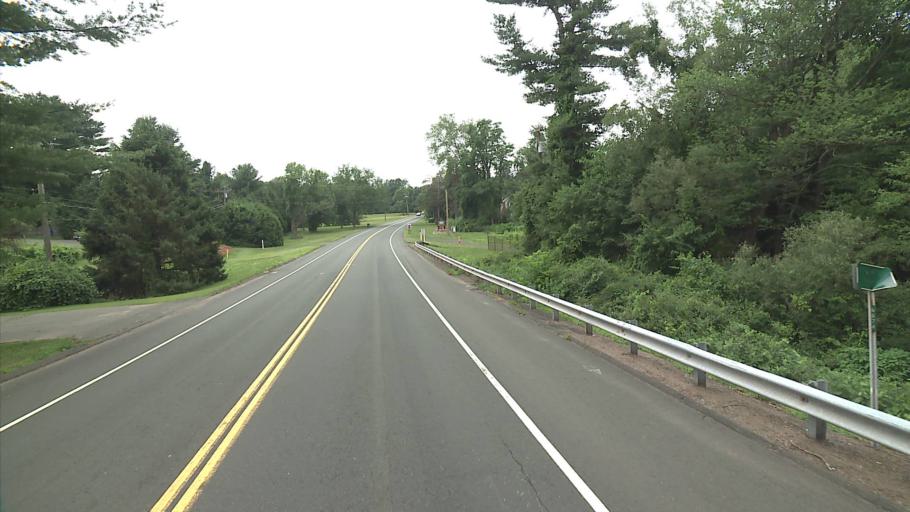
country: US
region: Connecticut
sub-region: Middlesex County
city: Cromwell
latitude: 41.6358
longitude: -72.6488
